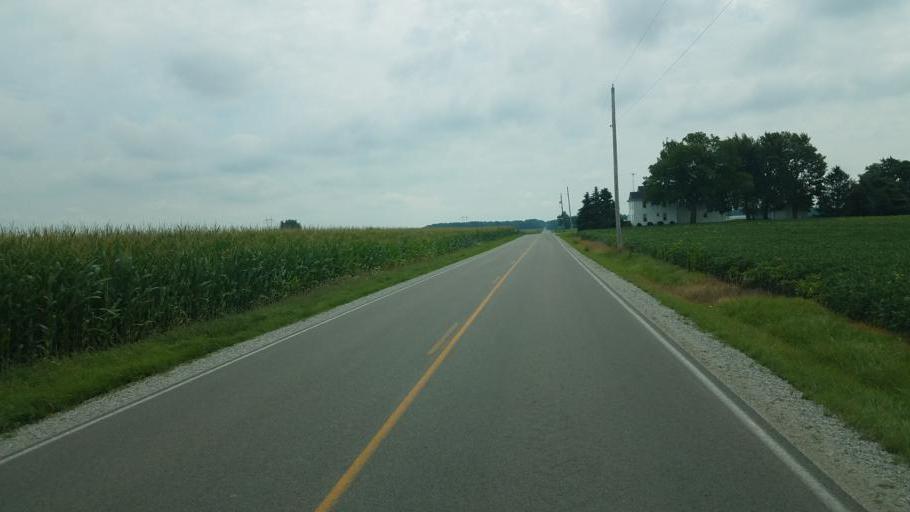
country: US
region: Ohio
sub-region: Crawford County
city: Galion
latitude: 40.7194
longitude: -82.8948
